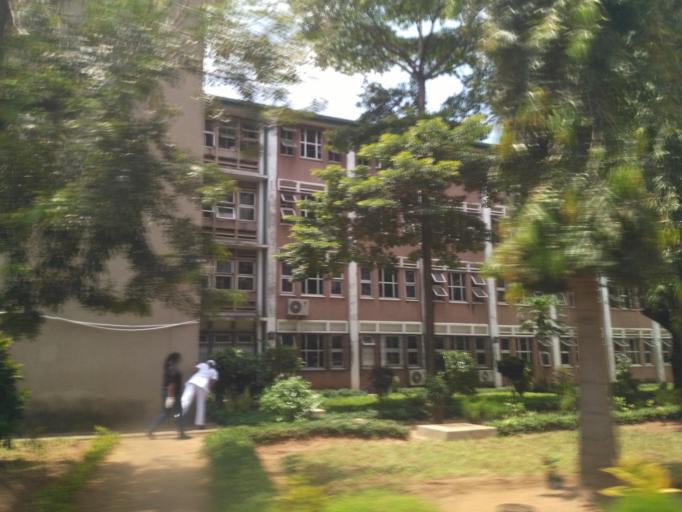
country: TZ
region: Dar es Salaam
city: Dar es Salaam
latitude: -6.8052
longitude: 39.2718
